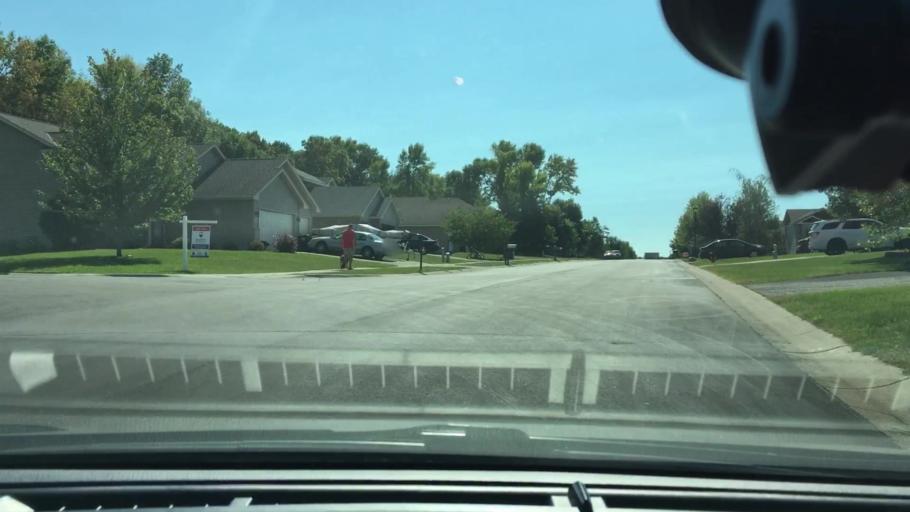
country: US
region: Minnesota
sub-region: Wright County
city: Saint Michael
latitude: 45.2041
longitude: -93.6758
